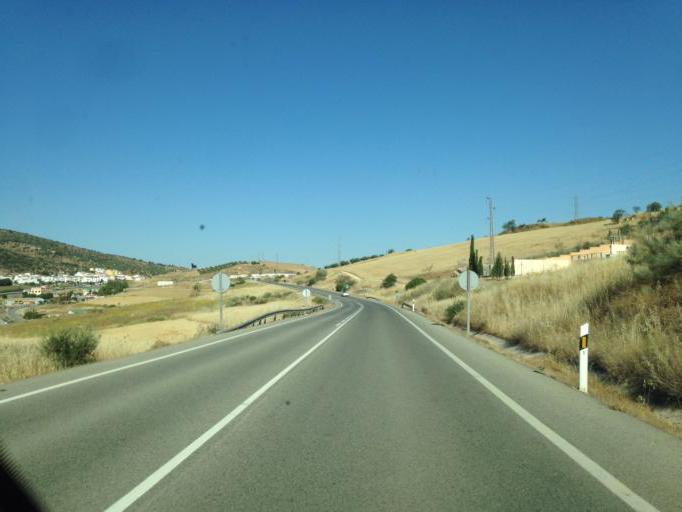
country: ES
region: Andalusia
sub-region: Provincia de Malaga
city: Casabermeja
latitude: 36.9007
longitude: -4.4197
